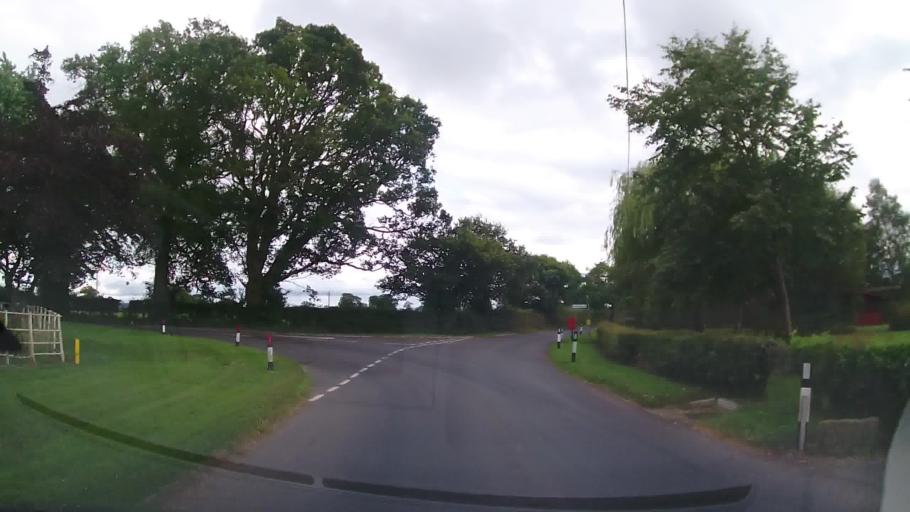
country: GB
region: England
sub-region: Shropshire
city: Wem
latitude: 52.8713
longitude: -2.7229
